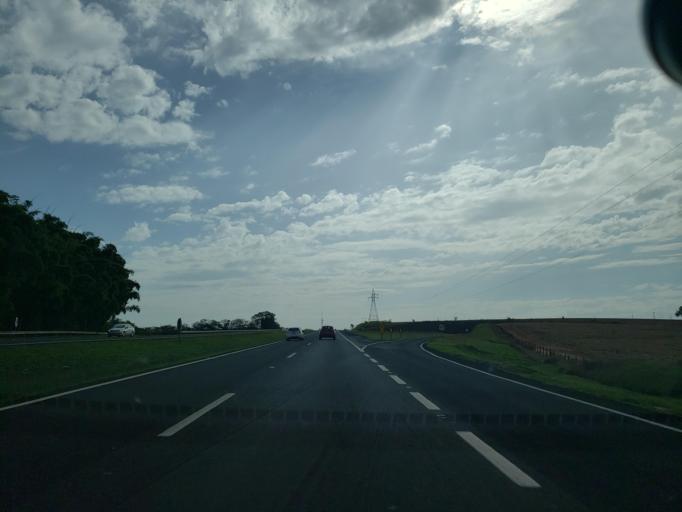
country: BR
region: Sao Paulo
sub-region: Lins
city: Lins
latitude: -21.7376
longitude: -49.7026
